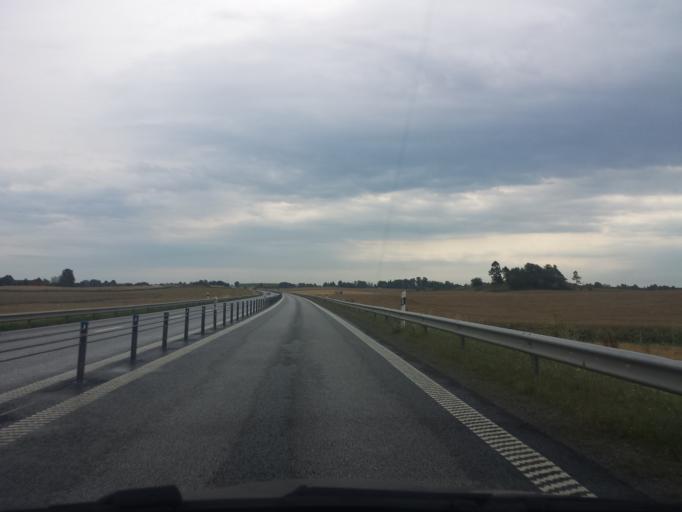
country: SE
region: Skane
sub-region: Skurups Kommun
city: Rydsgard
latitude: 55.4841
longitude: 13.5772
